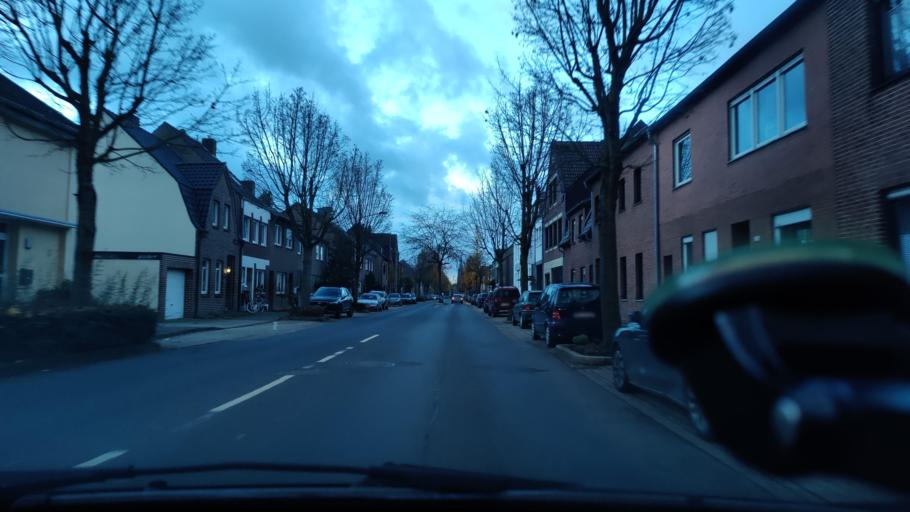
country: DE
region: North Rhine-Westphalia
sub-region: Regierungsbezirk Dusseldorf
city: Kevelaer
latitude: 51.5770
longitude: 6.2552
